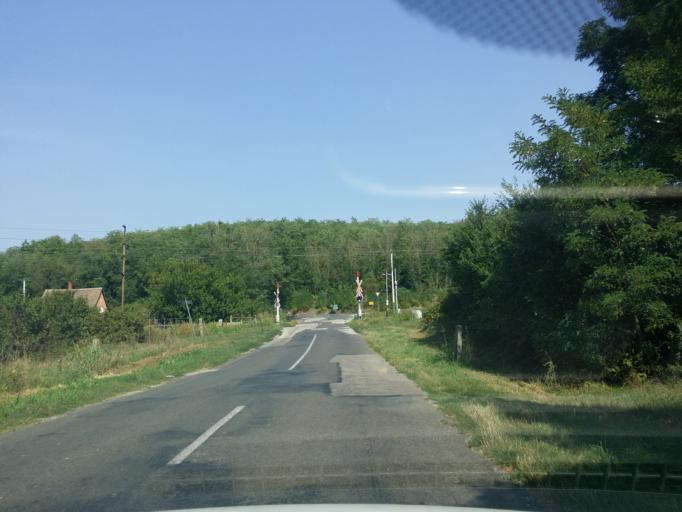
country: HU
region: Tolna
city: Gyonk
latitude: 46.5999
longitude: 18.4233
